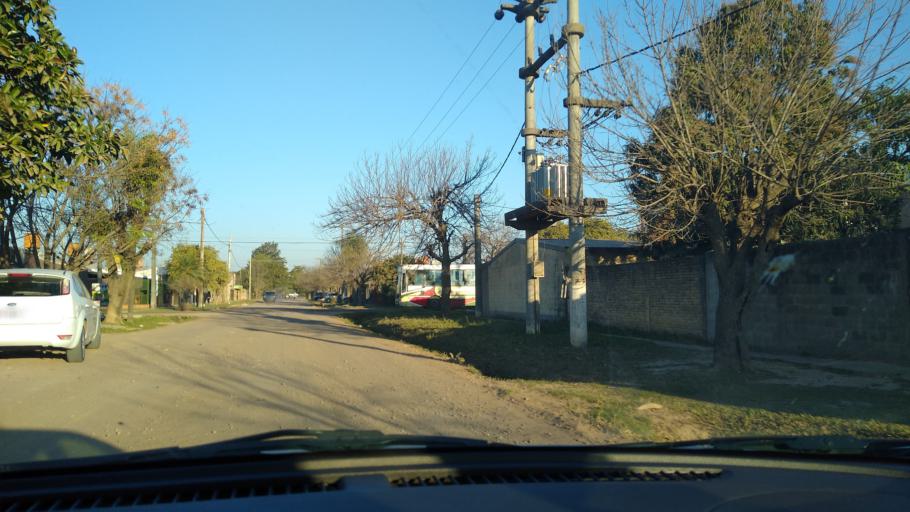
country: AR
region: Chaco
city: Resistencia
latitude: -27.4863
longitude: -58.9781
